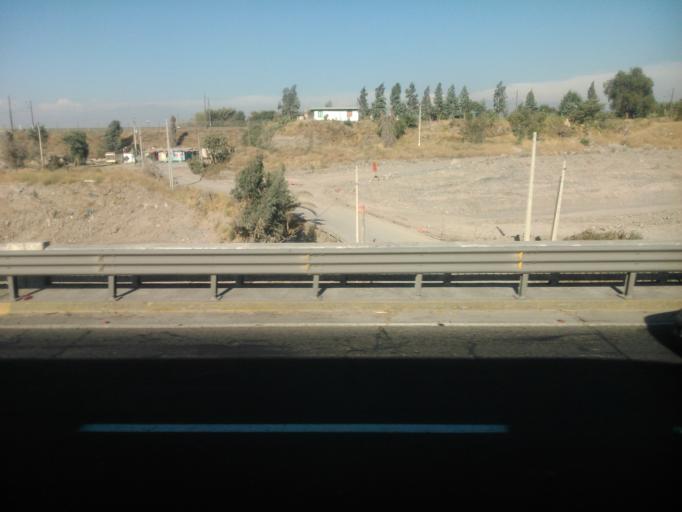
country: CL
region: Santiago Metropolitan
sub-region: Provincia de Maipo
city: Buin
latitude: -33.6923
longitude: -70.7231
